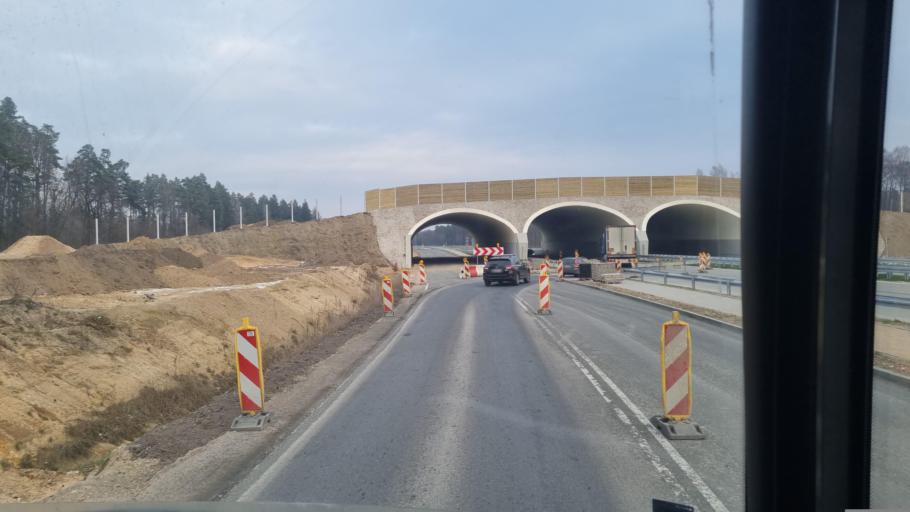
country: PL
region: Warmian-Masurian Voivodeship
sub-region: Powiat elcki
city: Elk
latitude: 53.8413
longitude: 22.4410
